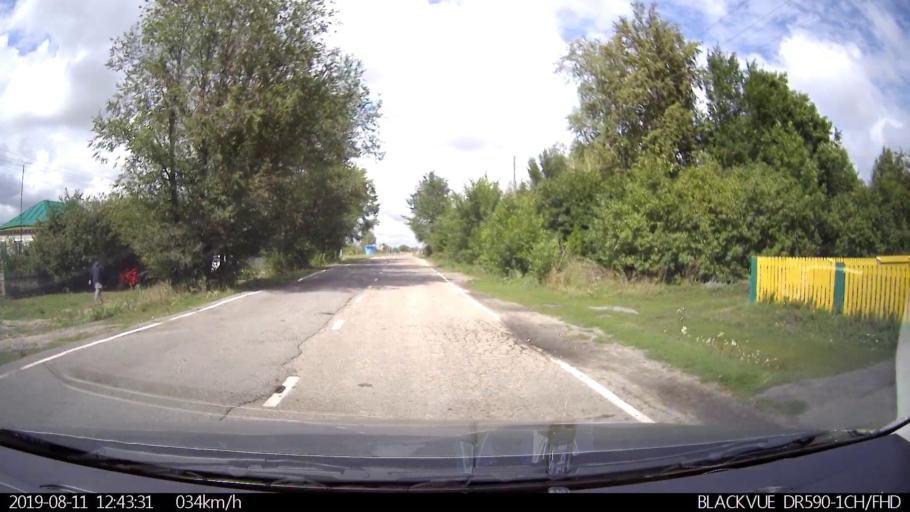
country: RU
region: Ulyanovsk
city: Ignatovka
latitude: 53.8510
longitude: 47.7425
